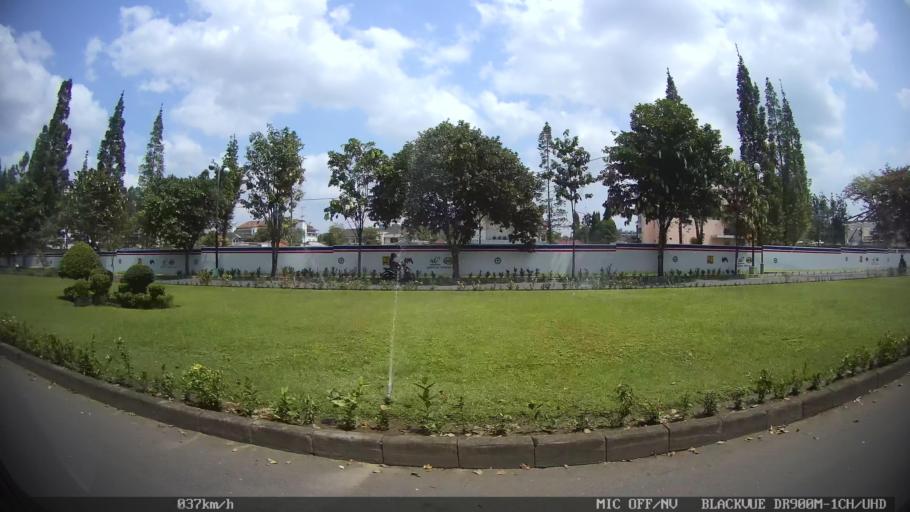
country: ID
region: Daerah Istimewa Yogyakarta
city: Yogyakarta
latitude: -7.7744
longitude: 110.3767
